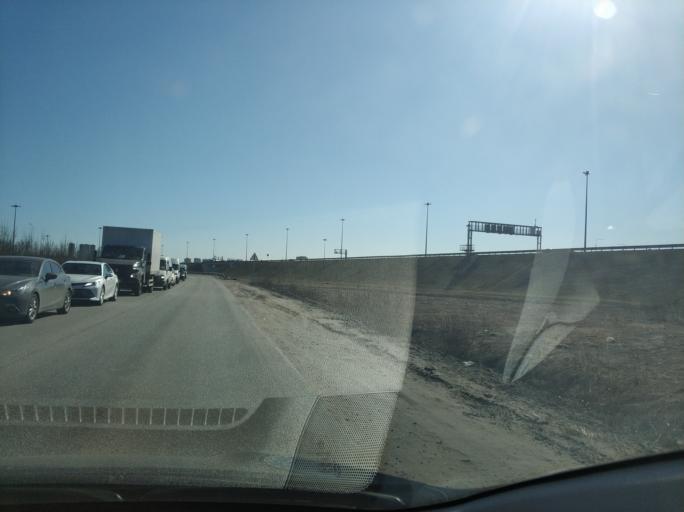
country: RU
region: Leningrad
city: Bugry
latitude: 60.0620
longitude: 30.3895
